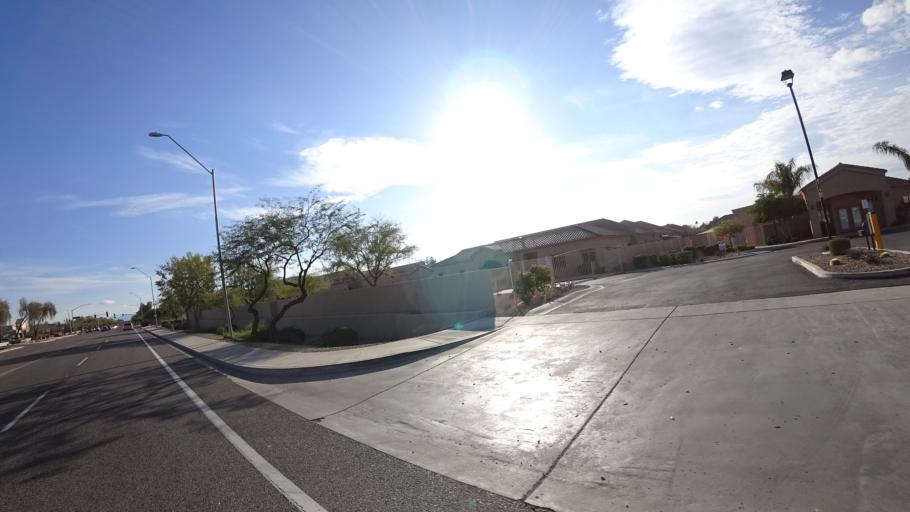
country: US
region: Arizona
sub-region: Maricopa County
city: Sun City
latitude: 33.6543
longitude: -112.2550
